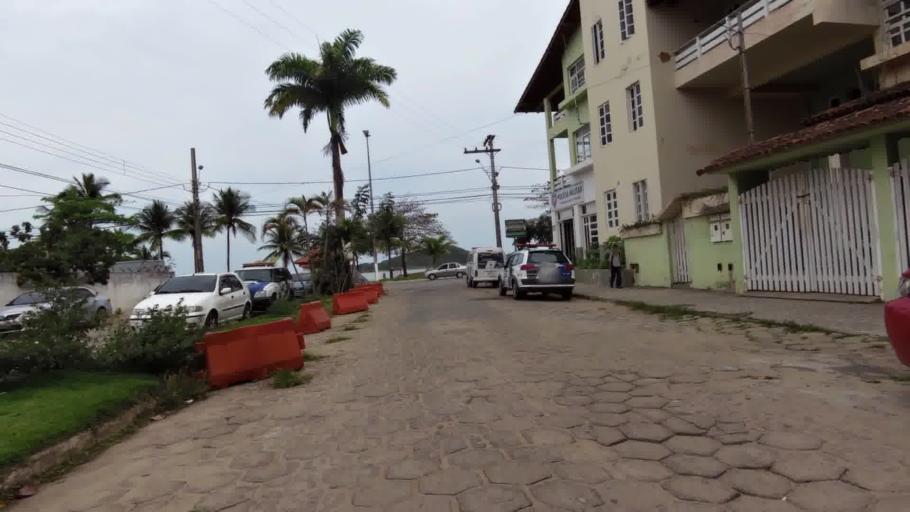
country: BR
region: Espirito Santo
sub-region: Piuma
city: Piuma
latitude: -20.8415
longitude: -40.7288
